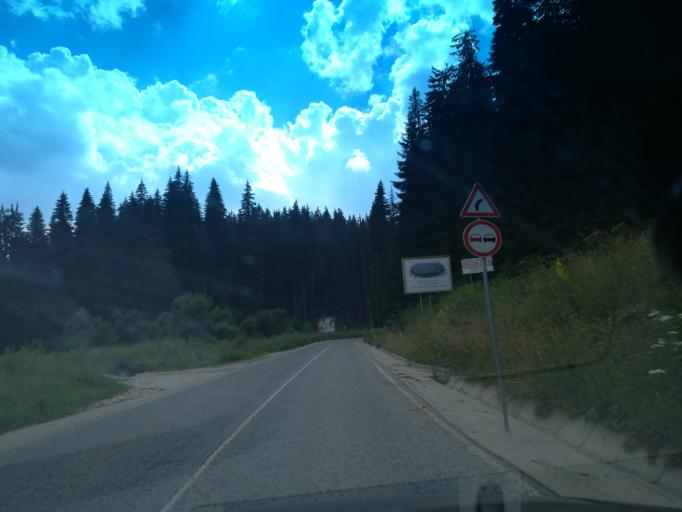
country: BG
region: Smolyan
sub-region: Obshtina Smolyan
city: Smolyan
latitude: 41.6586
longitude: 24.7119
